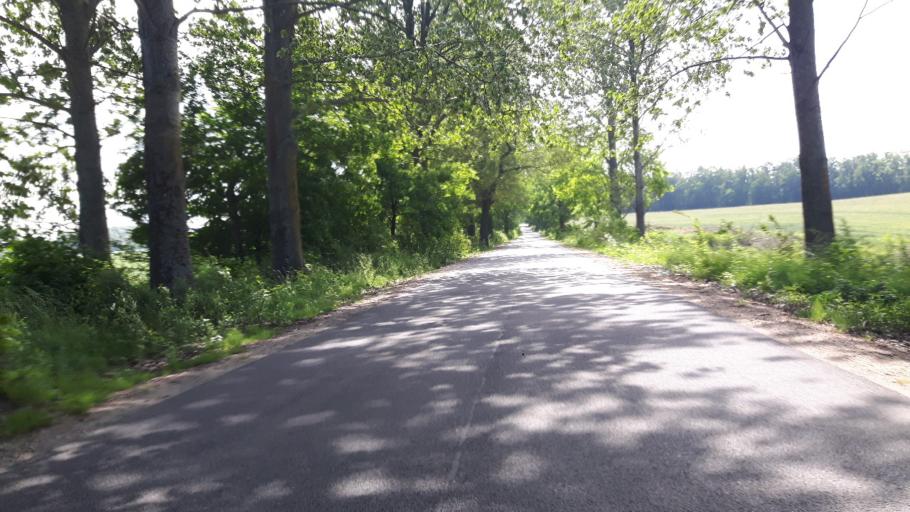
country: PL
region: Pomeranian Voivodeship
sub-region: Powiat wejherowski
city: Choczewo
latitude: 54.7525
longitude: 17.7928
